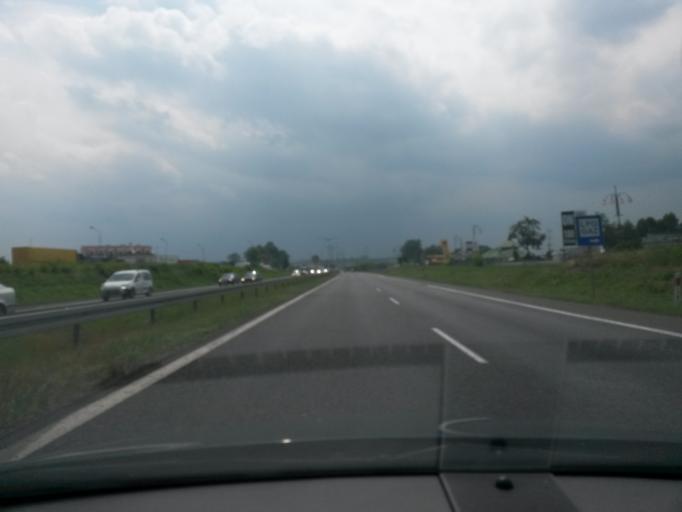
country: PL
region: Lodz Voivodeship
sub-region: Powiat radomszczanski
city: Radomsko
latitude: 51.1091
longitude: 19.3912
